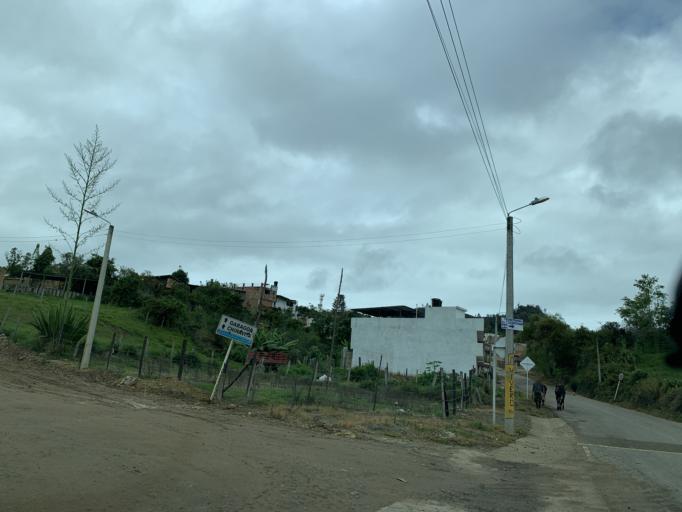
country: CO
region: Boyaca
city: Tibana
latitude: 5.3211
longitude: -73.3957
